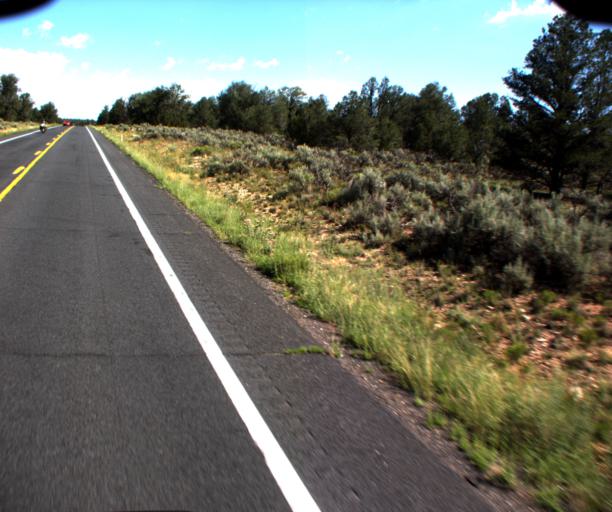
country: US
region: Arizona
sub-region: Coconino County
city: Grand Canyon Village
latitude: 35.8432
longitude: -112.1324
